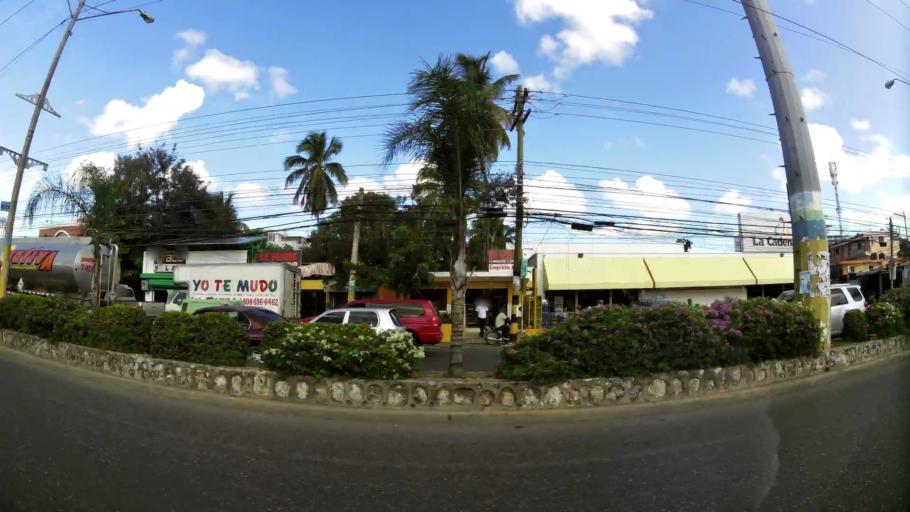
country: DO
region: Santo Domingo
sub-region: Santo Domingo
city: Santo Domingo Este
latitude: 18.5092
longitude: -69.8517
